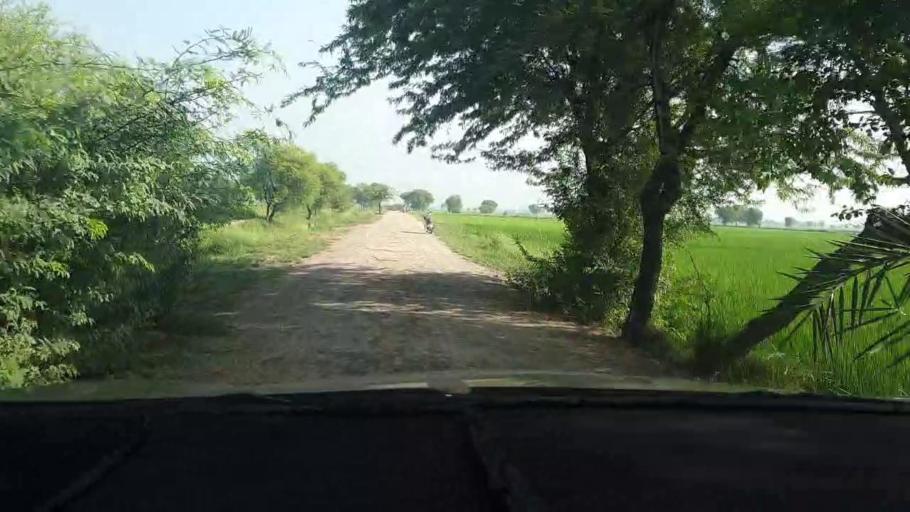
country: PK
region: Sindh
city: Kambar
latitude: 27.5852
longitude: 68.1023
